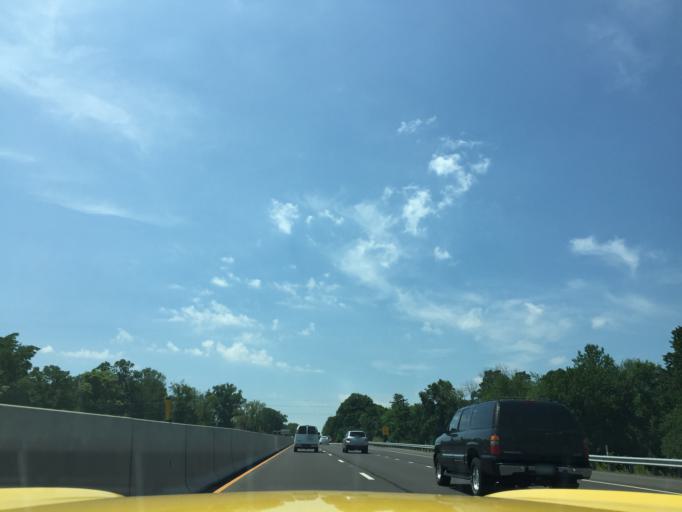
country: US
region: Pennsylvania
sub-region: Bucks County
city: Langhorne Manor
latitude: 40.1800
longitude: -74.9048
